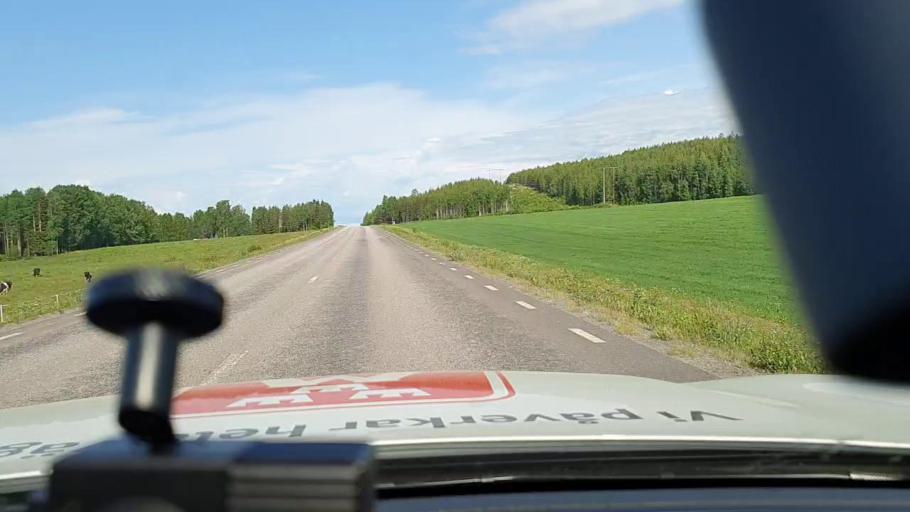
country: SE
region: Norrbotten
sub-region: Bodens Kommun
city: Boden
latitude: 65.9128
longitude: 21.3444
